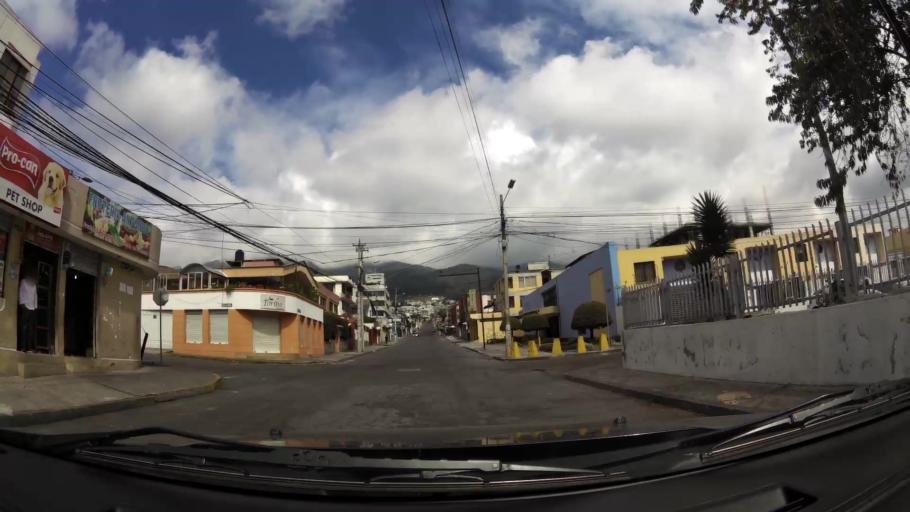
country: EC
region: Pichincha
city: Quito
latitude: -0.1459
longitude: -78.4931
